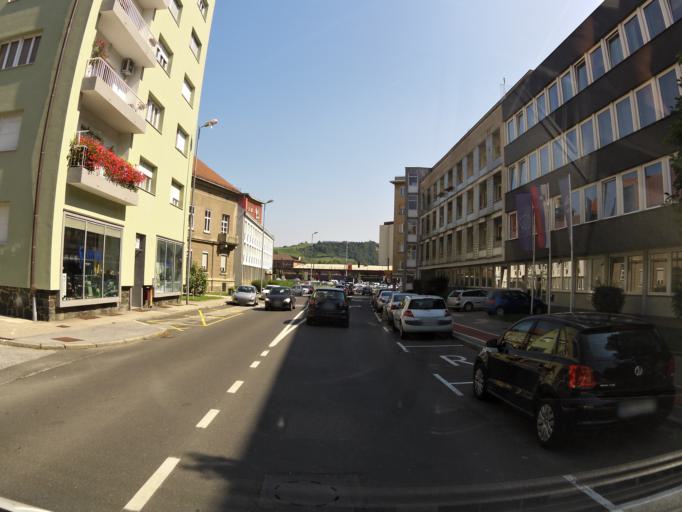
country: SI
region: Maribor
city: Maribor
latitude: 46.5631
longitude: 15.6564
